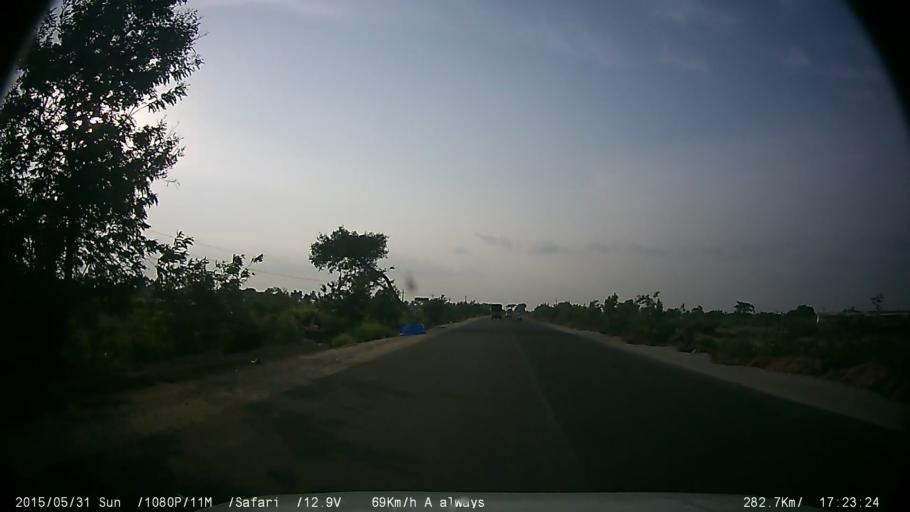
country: IN
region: Karnataka
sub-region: Chamrajnagar
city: Gundlupet
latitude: 11.8394
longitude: 76.6745
